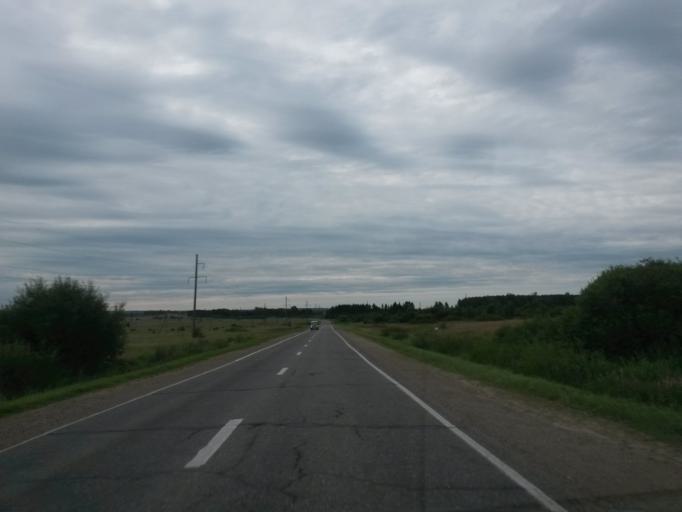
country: RU
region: Jaroslavl
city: Gavrilov-Yam
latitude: 57.3523
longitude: 39.7874
